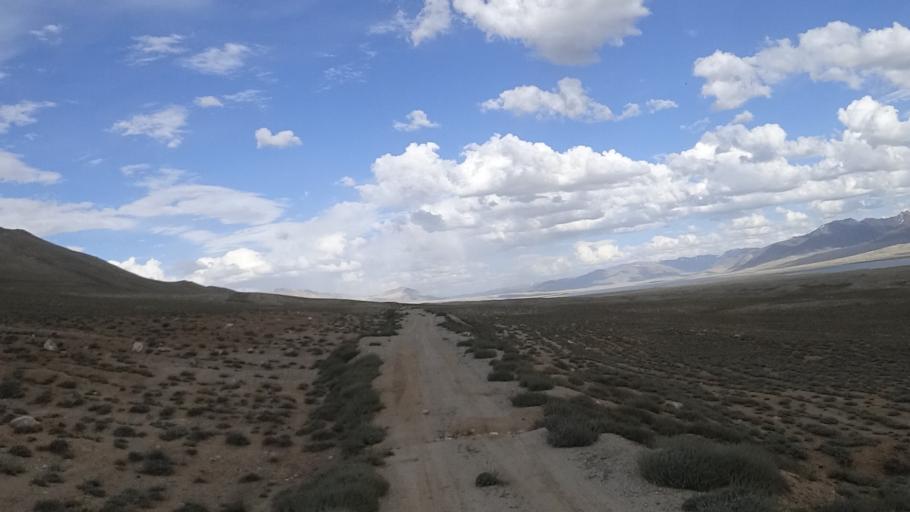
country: TJ
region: Gorno-Badakhshan
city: Murghob
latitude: 37.4682
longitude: 73.5735
